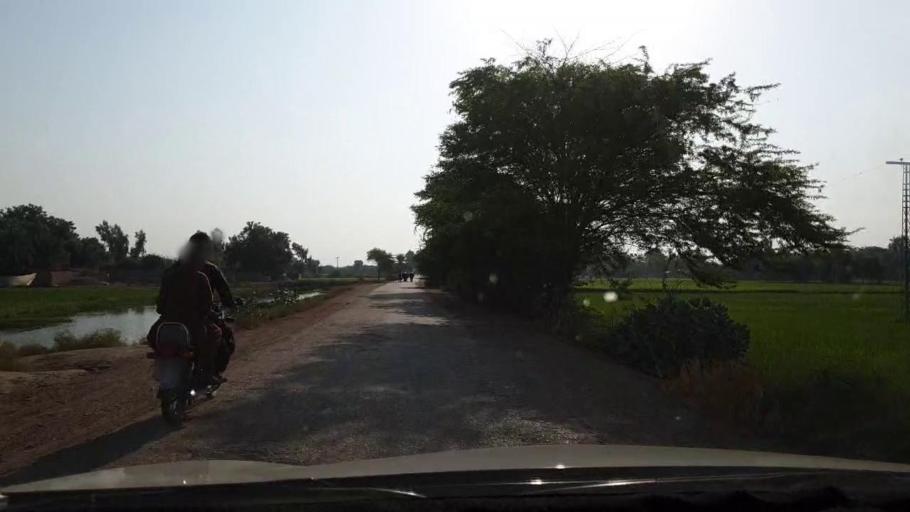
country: PK
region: Sindh
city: Larkana
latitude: 27.5513
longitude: 68.2581
